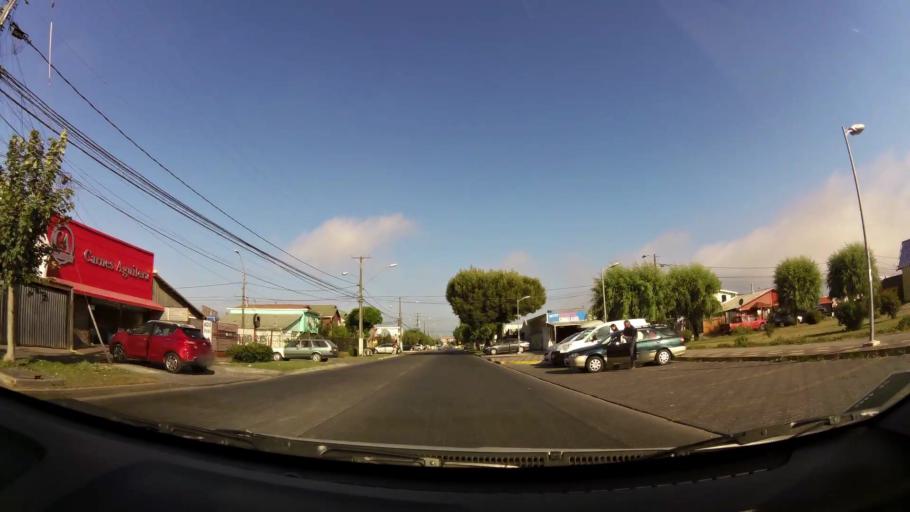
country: CL
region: Biobio
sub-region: Provincia de Concepcion
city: Concepcion
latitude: -36.7931
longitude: -73.1044
